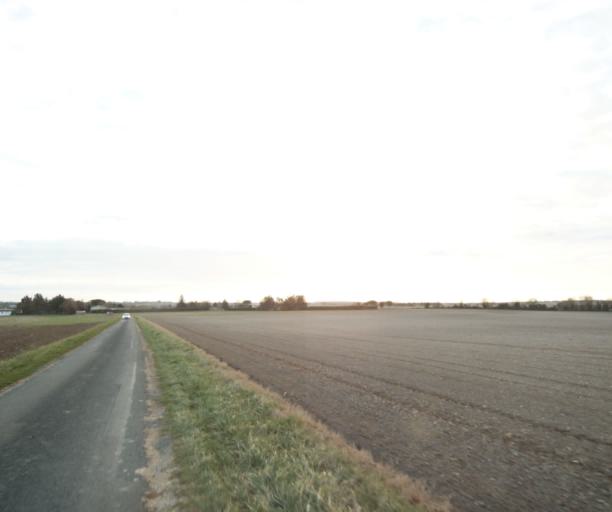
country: FR
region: Poitou-Charentes
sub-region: Departement de la Charente-Maritime
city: Les Gonds
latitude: 45.7013
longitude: -0.6172
